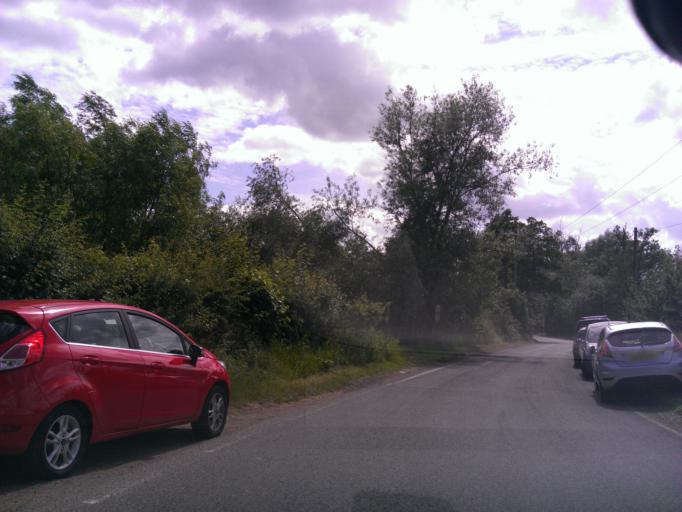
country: GB
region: England
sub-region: Essex
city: Hatfield Peverel
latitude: 51.7526
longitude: 0.5741
